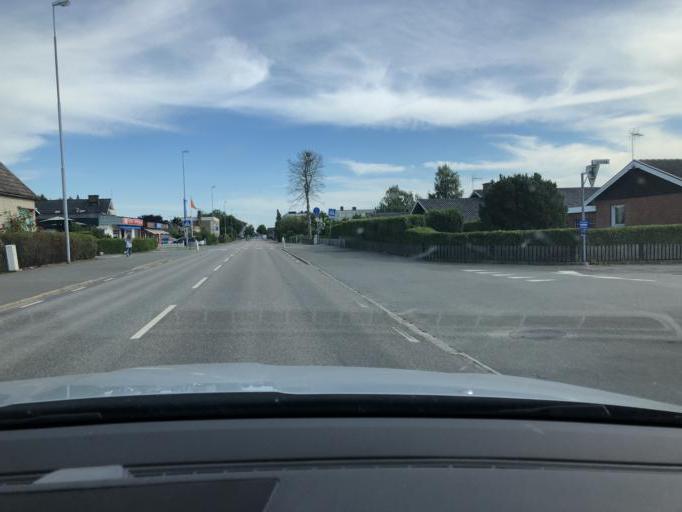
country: SE
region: Skane
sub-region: Bromolla Kommun
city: Bromoella
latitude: 56.0726
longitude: 14.4767
